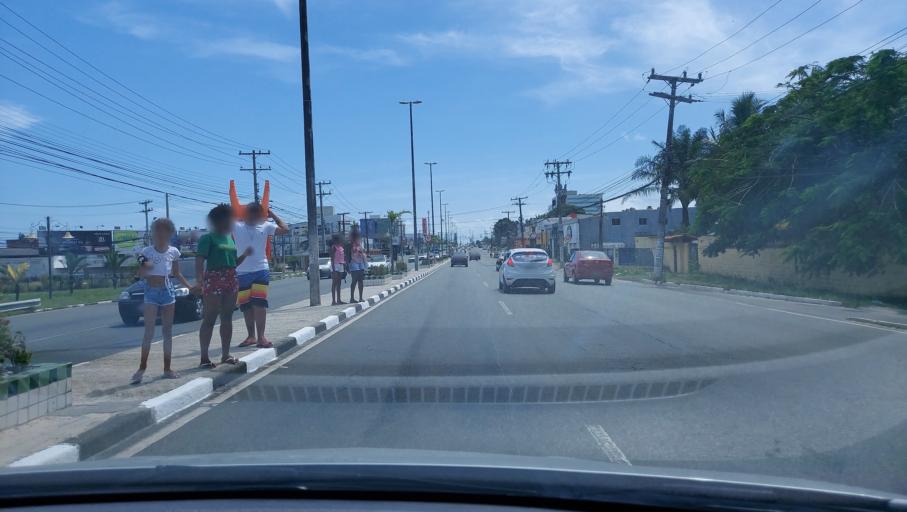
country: BR
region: Bahia
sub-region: Lauro De Freitas
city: Lauro de Freitas
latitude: -12.8727
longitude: -38.3043
